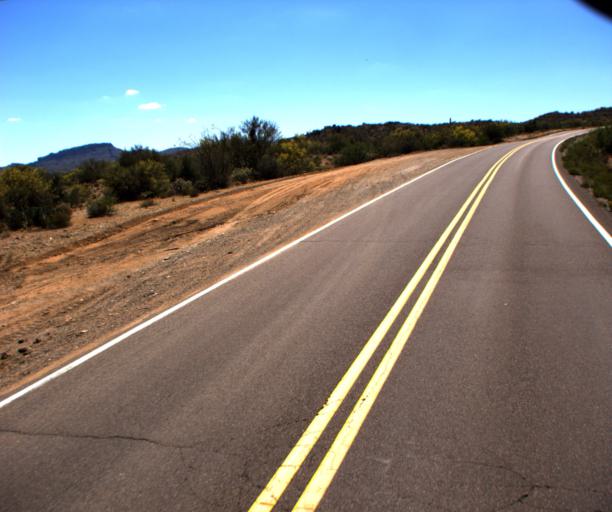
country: US
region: Arizona
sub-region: Yavapai County
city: Bagdad
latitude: 34.4608
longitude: -113.2391
